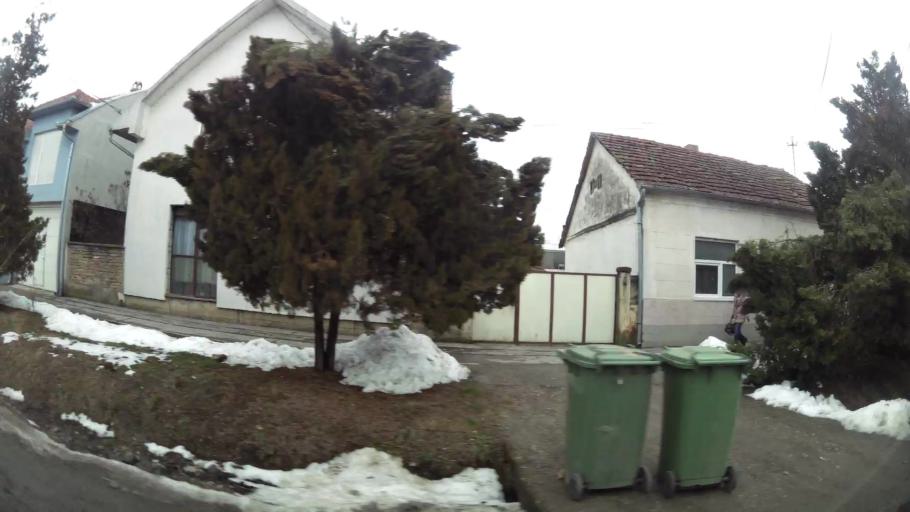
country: RS
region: Central Serbia
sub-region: Belgrade
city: Surcin
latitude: 44.7921
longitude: 20.2695
